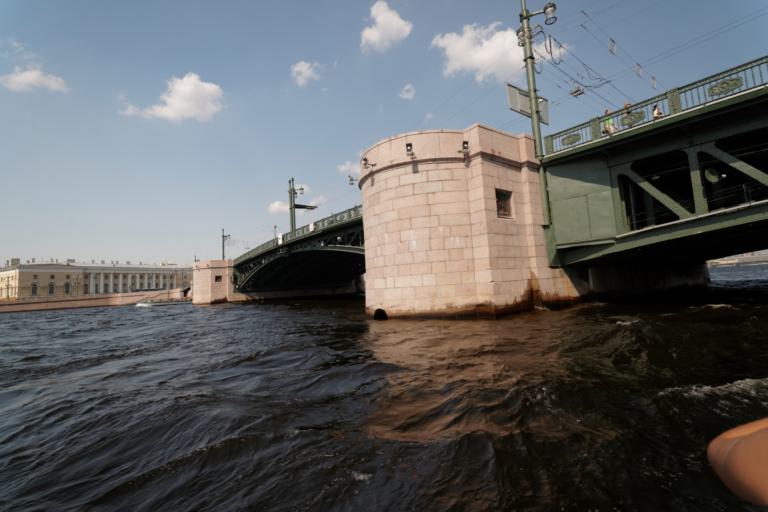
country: RU
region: St.-Petersburg
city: Saint Petersburg
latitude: 59.9406
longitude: 30.3082
